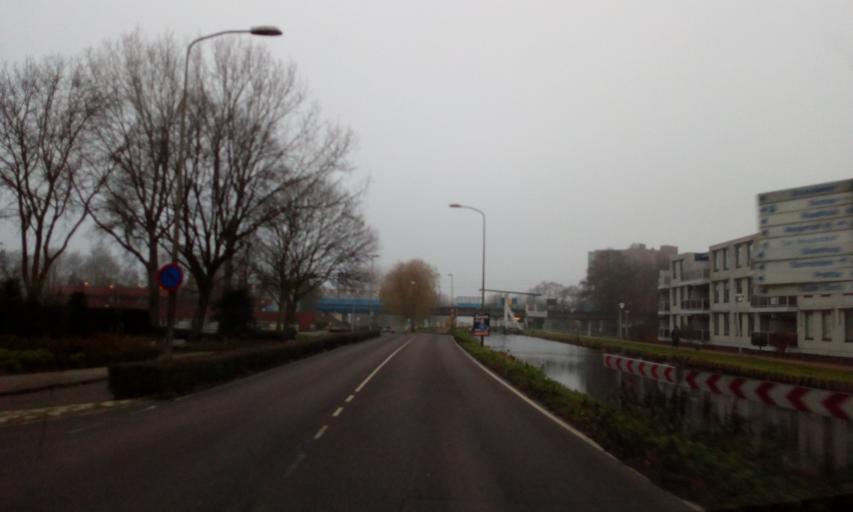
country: NL
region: South Holland
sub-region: Gemeente Krimpen aan den IJssel
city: Krimpen aan den IJssel
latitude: 51.9648
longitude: 4.6195
